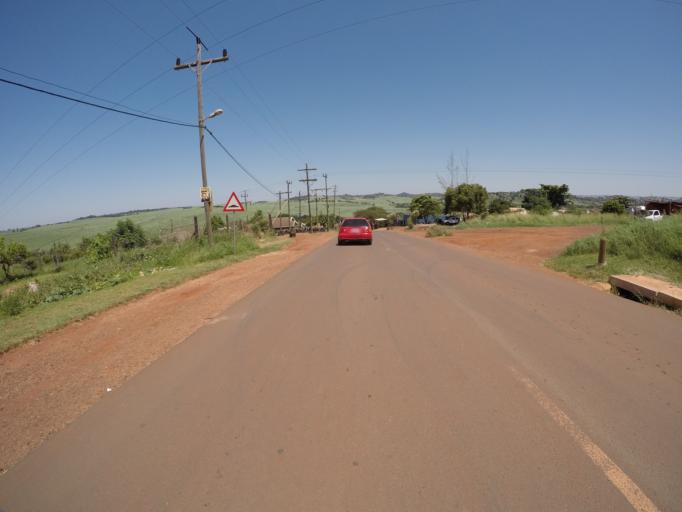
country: ZA
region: KwaZulu-Natal
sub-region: uThungulu District Municipality
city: Empangeni
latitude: -28.7753
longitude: 31.8819
